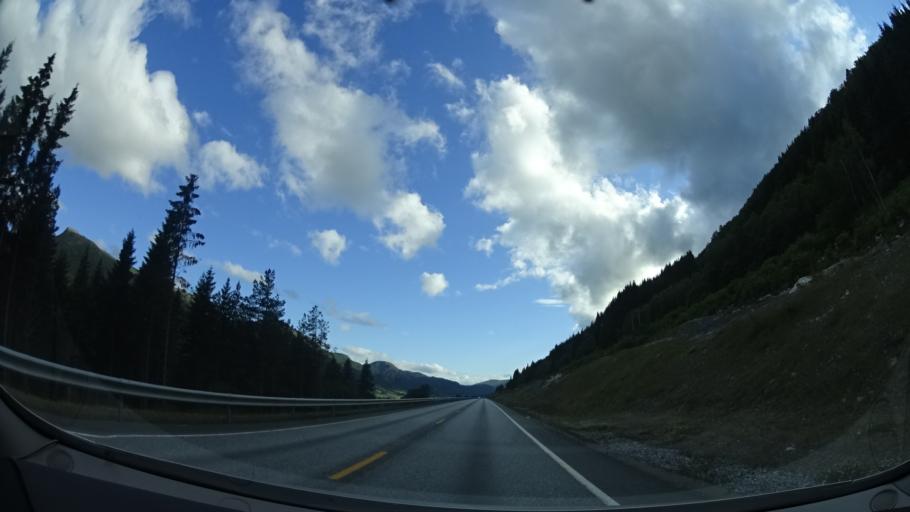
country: NO
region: More og Romsdal
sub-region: Gjemnes
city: Batnfjordsora
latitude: 62.9177
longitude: 7.6949
